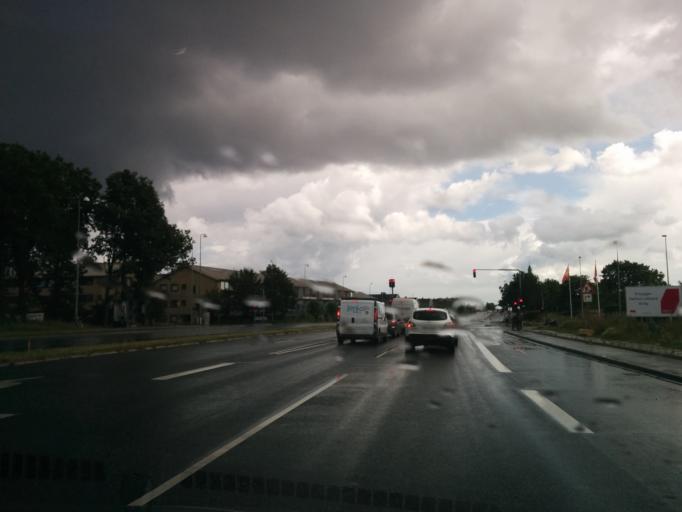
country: DK
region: Central Jutland
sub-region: Arhus Kommune
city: Arhus
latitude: 56.1874
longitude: 10.1937
